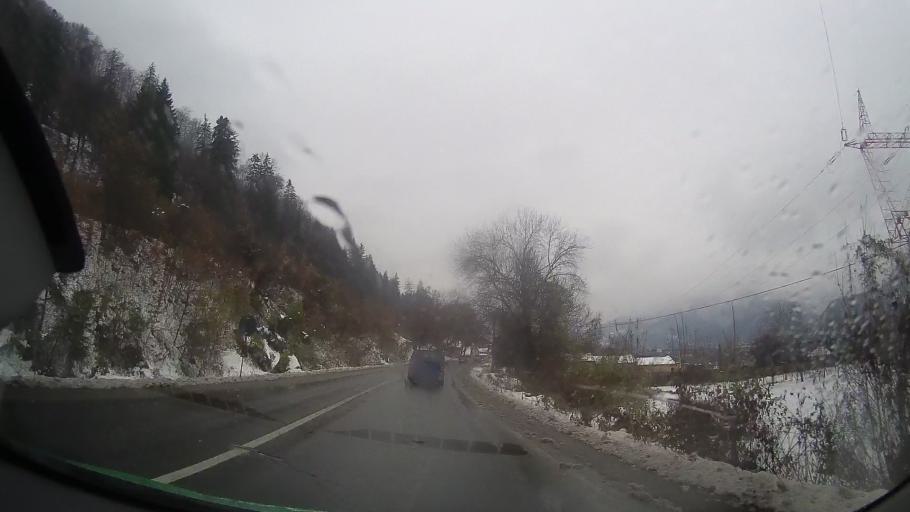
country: RO
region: Neamt
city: Viisoara
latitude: 46.9281
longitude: 26.2375
